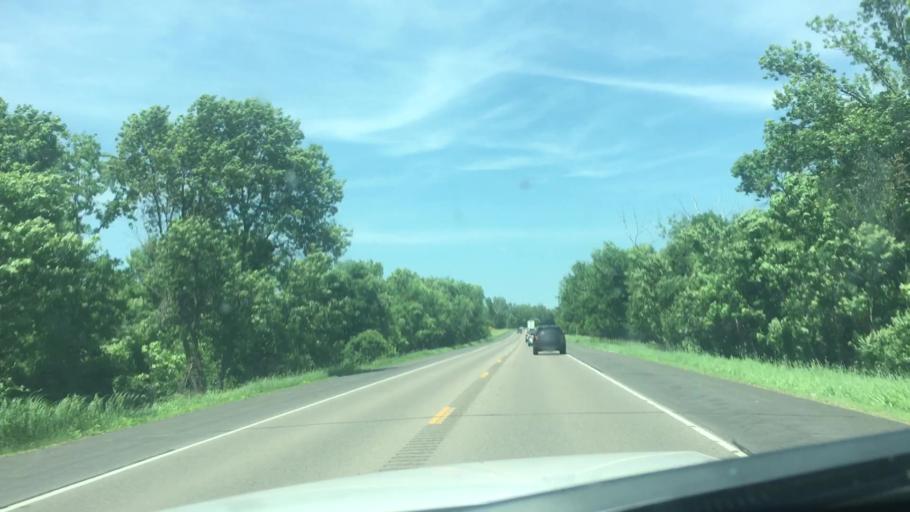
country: US
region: Minnesota
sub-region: Ramsey County
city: White Bear Lake
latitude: 45.1136
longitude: -93.0008
